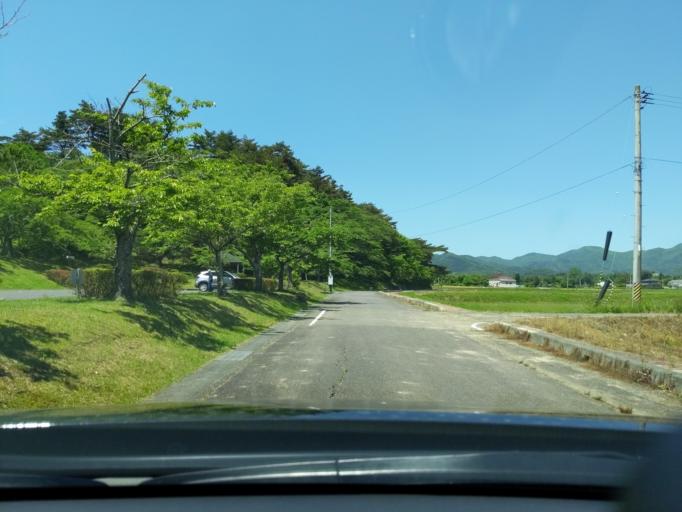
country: JP
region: Fukushima
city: Koriyama
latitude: 37.3895
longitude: 140.2765
